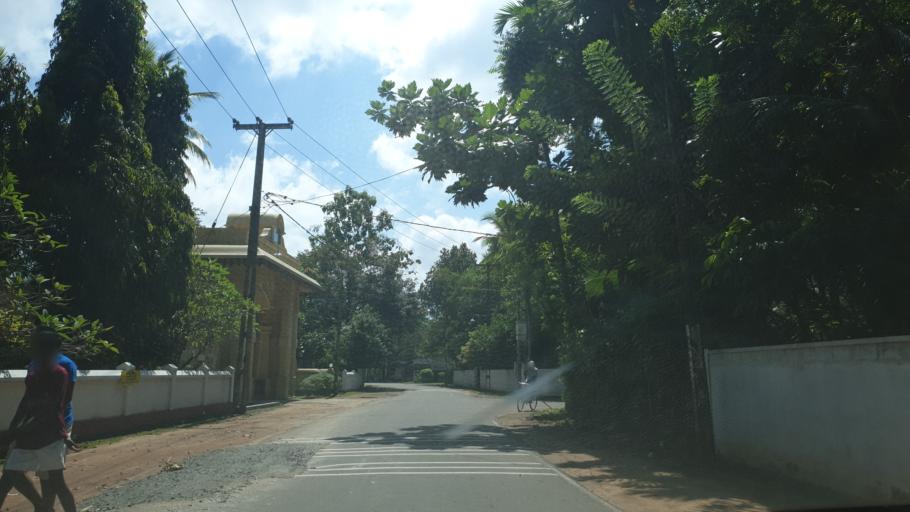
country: LK
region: Western
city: Panadura
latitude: 6.6768
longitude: 79.9305
